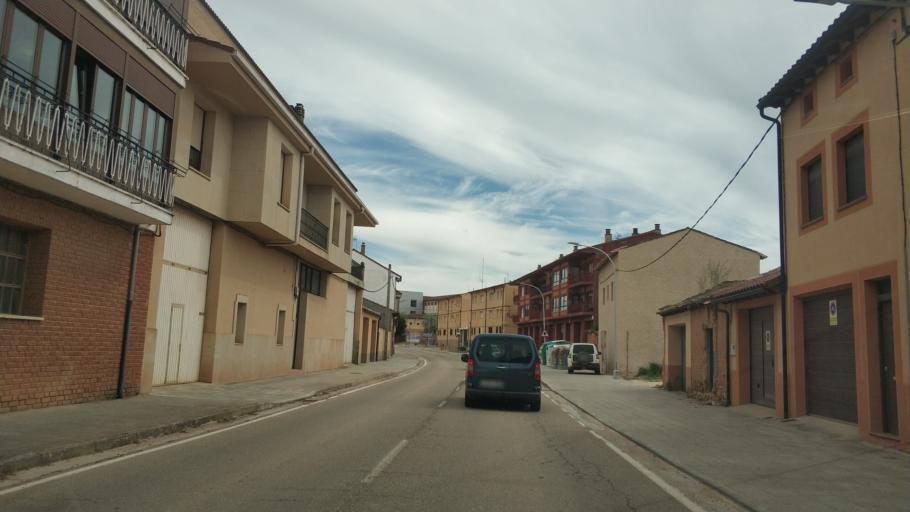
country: ES
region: Castille and Leon
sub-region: Provincia de Soria
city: Berlanga de Duero
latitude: 41.4663
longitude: -2.8630
